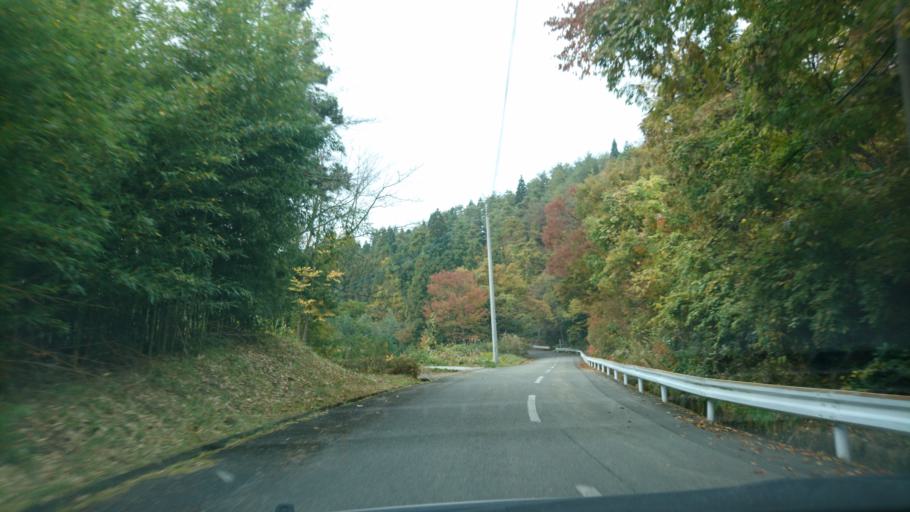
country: JP
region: Iwate
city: Ichinoseki
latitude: 38.9781
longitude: 141.1678
